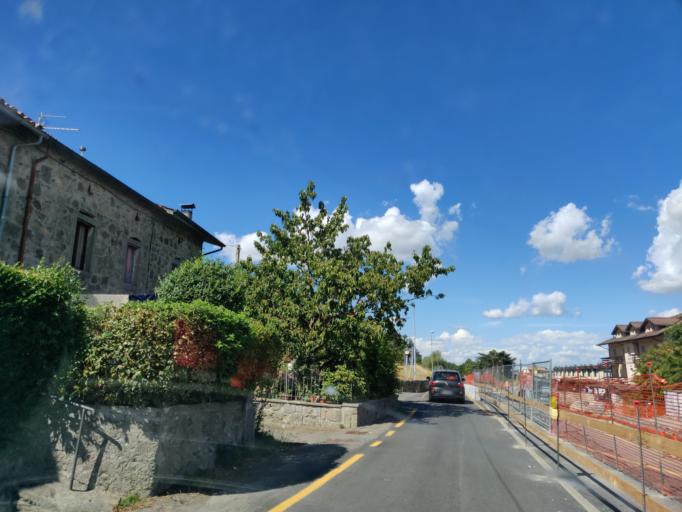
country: IT
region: Tuscany
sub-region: Provincia di Siena
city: Abbadia San Salvatore
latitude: 42.8899
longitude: 11.6663
